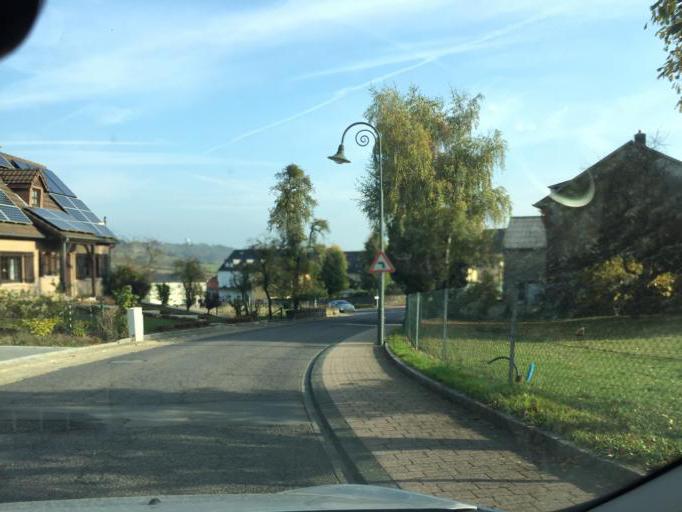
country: LU
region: Luxembourg
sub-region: Canton de Luxembourg
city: Contern
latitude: 49.5635
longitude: 6.2180
